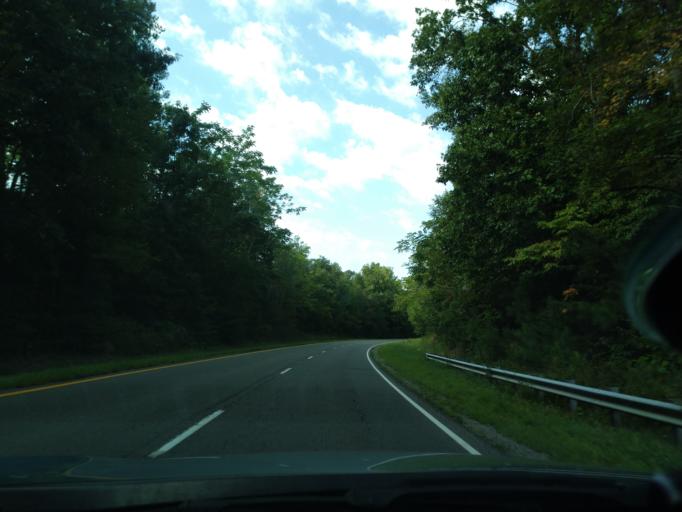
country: US
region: Virginia
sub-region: King George County
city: King George
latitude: 38.1470
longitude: -77.2172
